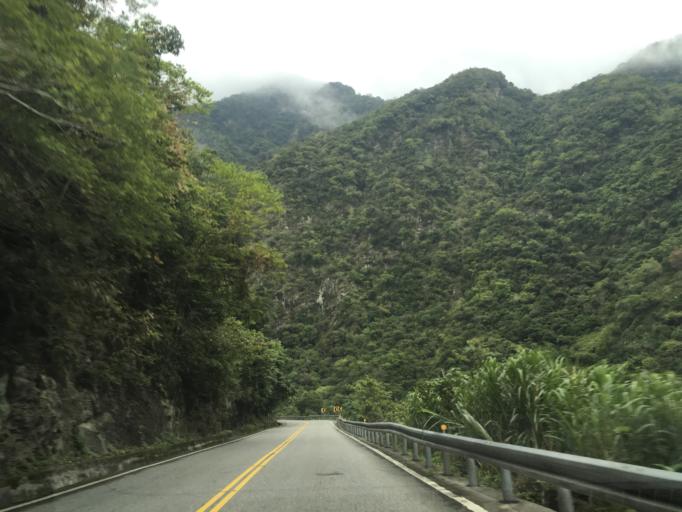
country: TW
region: Taiwan
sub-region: Hualien
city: Hualian
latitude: 24.1744
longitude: 121.5873
